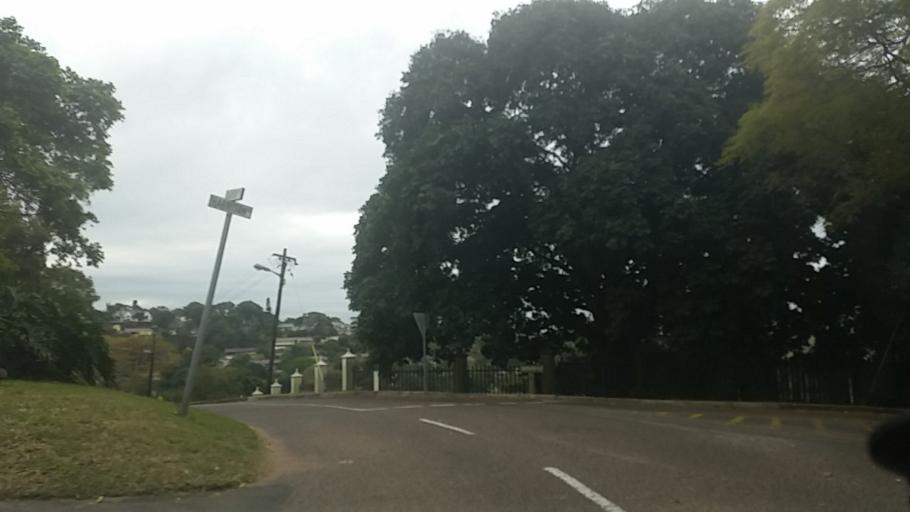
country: ZA
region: KwaZulu-Natal
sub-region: eThekwini Metropolitan Municipality
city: Berea
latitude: -29.8436
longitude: 30.9330
